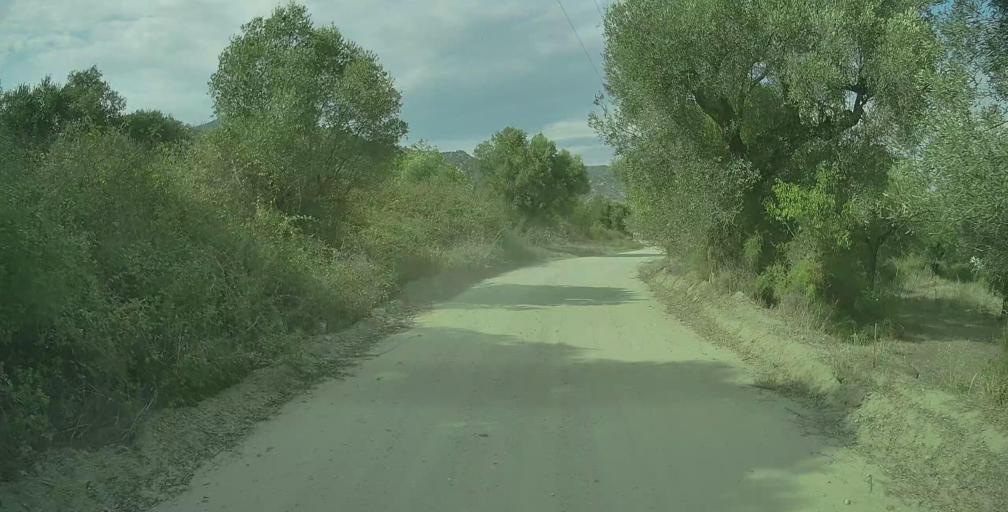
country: GR
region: Central Macedonia
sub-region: Nomos Chalkidikis
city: Sykia
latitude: 40.0285
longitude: 23.9447
